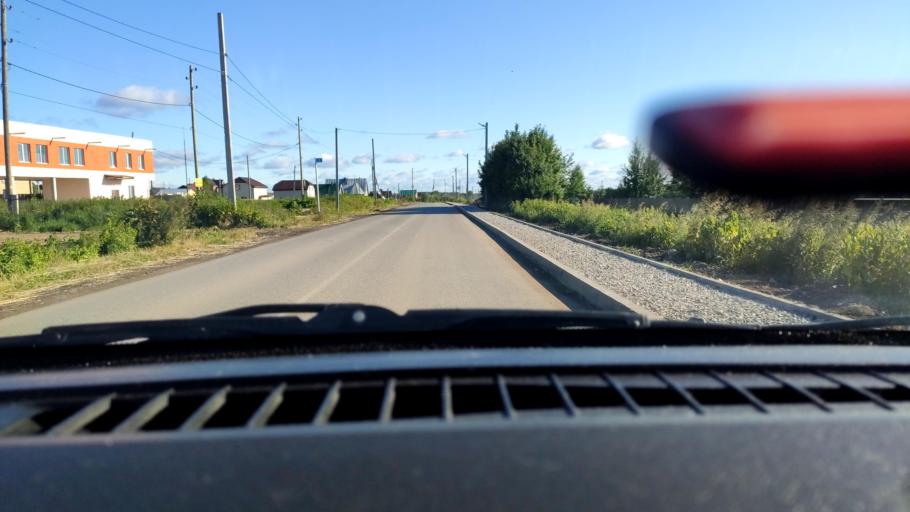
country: RU
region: Perm
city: Kultayevo
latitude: 57.8655
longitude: 55.9157
